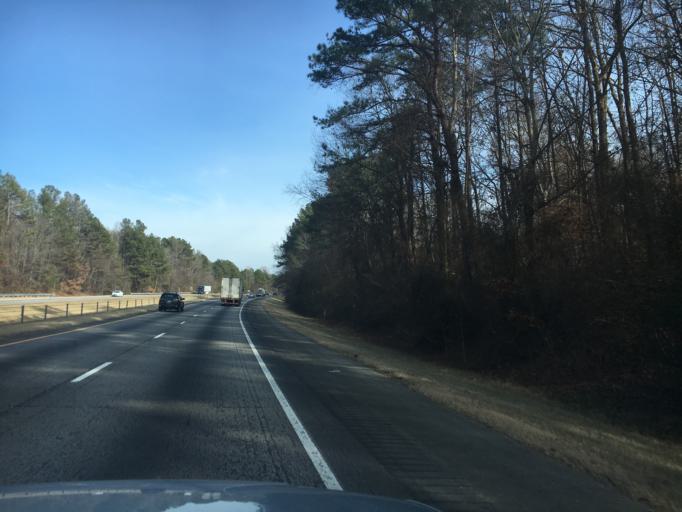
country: US
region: Georgia
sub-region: Jackson County
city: Braselton
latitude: 34.1252
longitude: -83.7412
